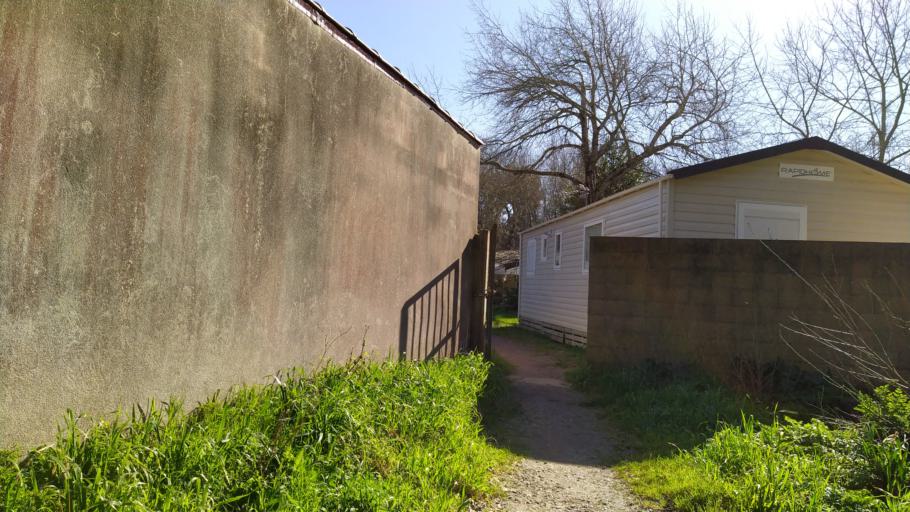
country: FR
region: Pays de la Loire
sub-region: Departement de la Loire-Atlantique
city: Saint-Michel-Chef-Chef
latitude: 47.2140
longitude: -2.1586
